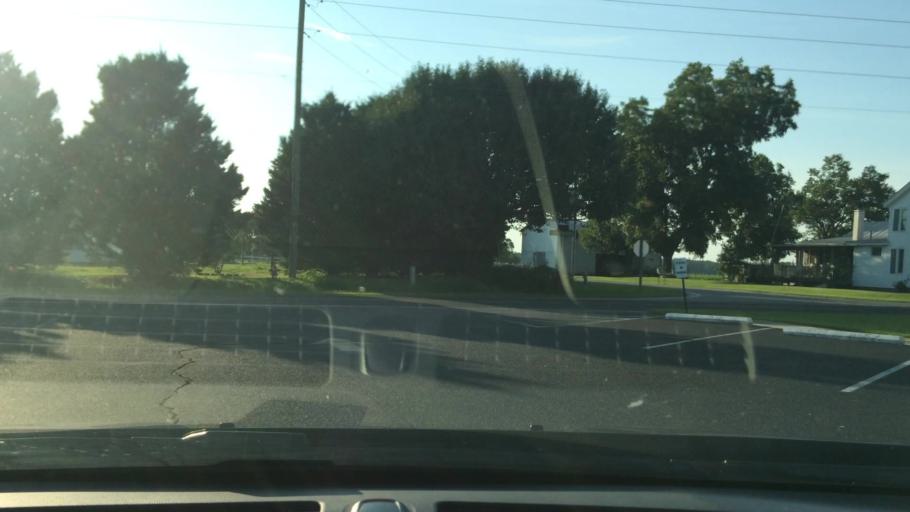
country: US
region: North Carolina
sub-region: Pitt County
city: Ayden
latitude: 35.4303
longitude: -77.4108
